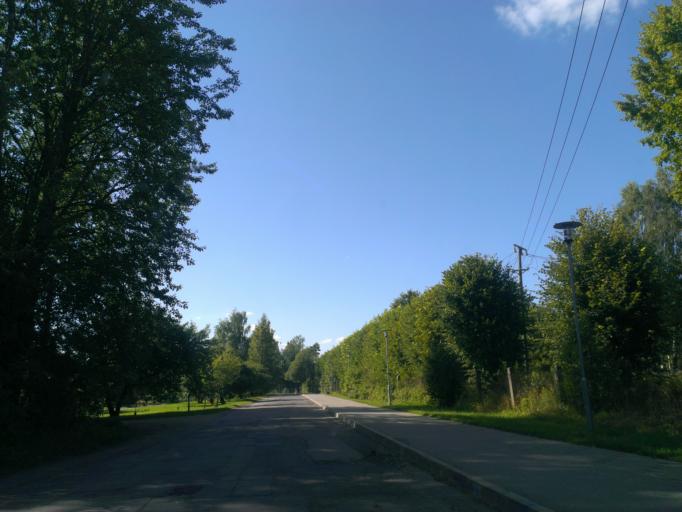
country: LV
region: Sigulda
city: Sigulda
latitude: 57.1634
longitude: 24.8795
